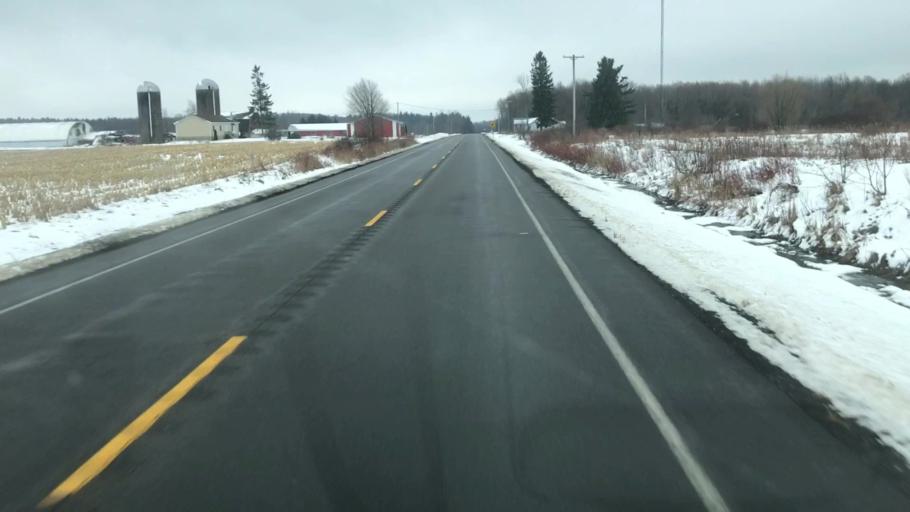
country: US
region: New York
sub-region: Cayuga County
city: Moravia
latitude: 42.7626
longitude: -76.3316
